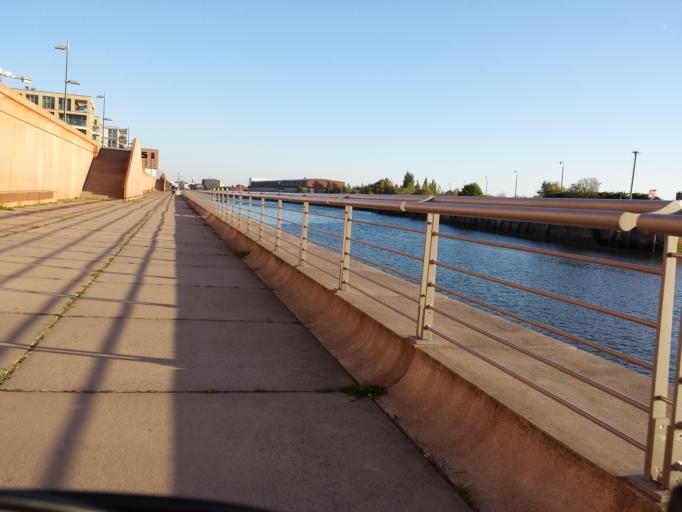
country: DE
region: Bremen
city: Bremen
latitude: 53.0963
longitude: 8.7621
